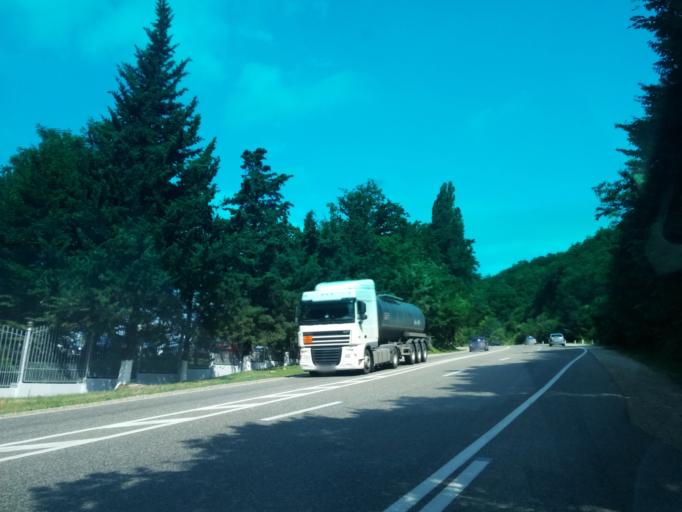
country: RU
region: Krasnodarskiy
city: Agoy
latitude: 44.1513
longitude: 39.0149
